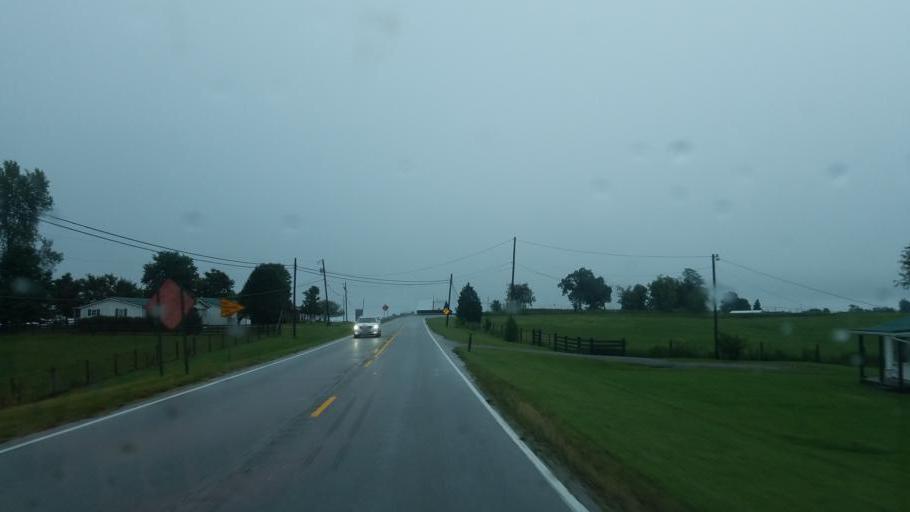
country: US
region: Kentucky
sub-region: Fleming County
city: Flemingsburg
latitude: 38.3968
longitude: -83.7025
